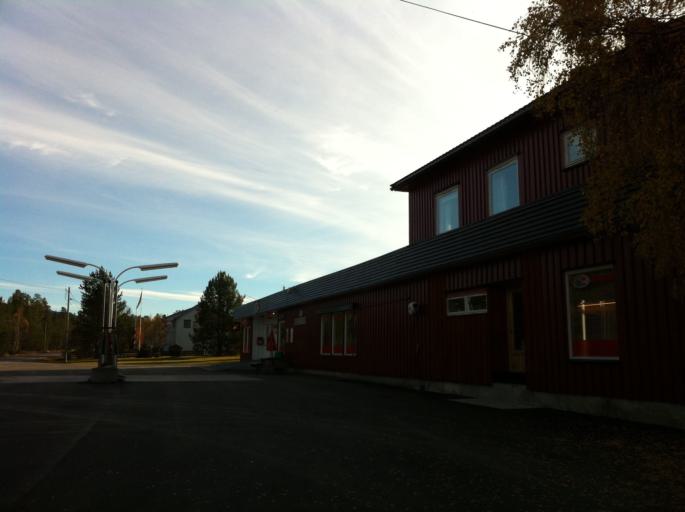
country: NO
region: Hedmark
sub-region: Engerdal
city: Engerdal
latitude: 62.1634
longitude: 11.9442
